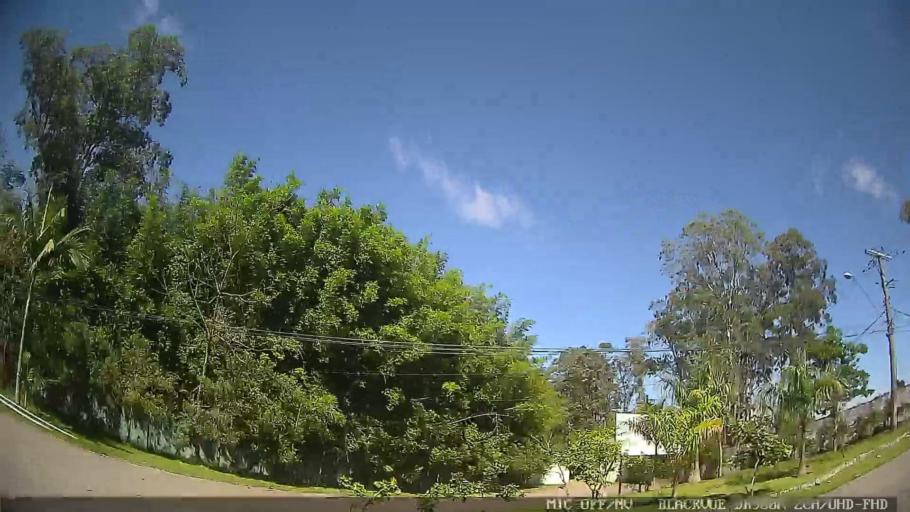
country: BR
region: Sao Paulo
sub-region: Suzano
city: Suzano
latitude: -23.5869
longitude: -46.2564
